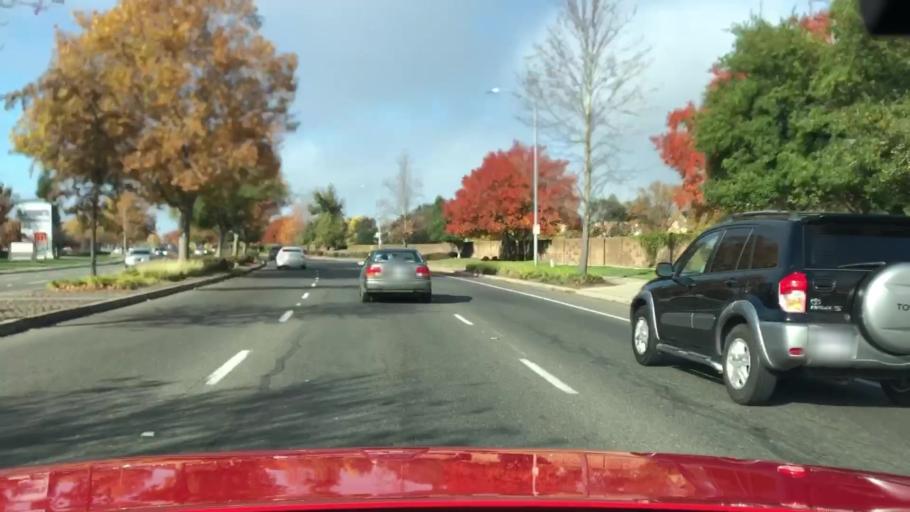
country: US
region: California
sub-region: Sacramento County
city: Laguna
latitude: 38.4553
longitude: -121.4009
